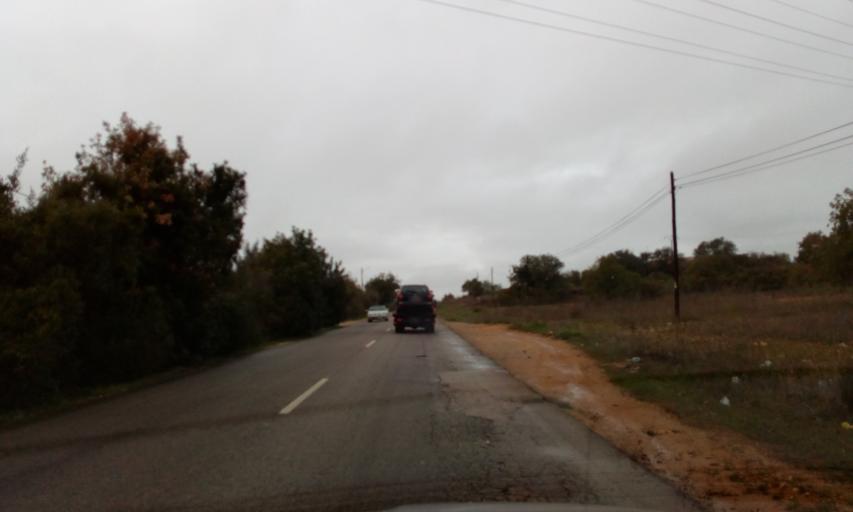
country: PT
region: Faro
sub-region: Albufeira
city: Ferreiras
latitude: 37.1363
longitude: -8.2641
